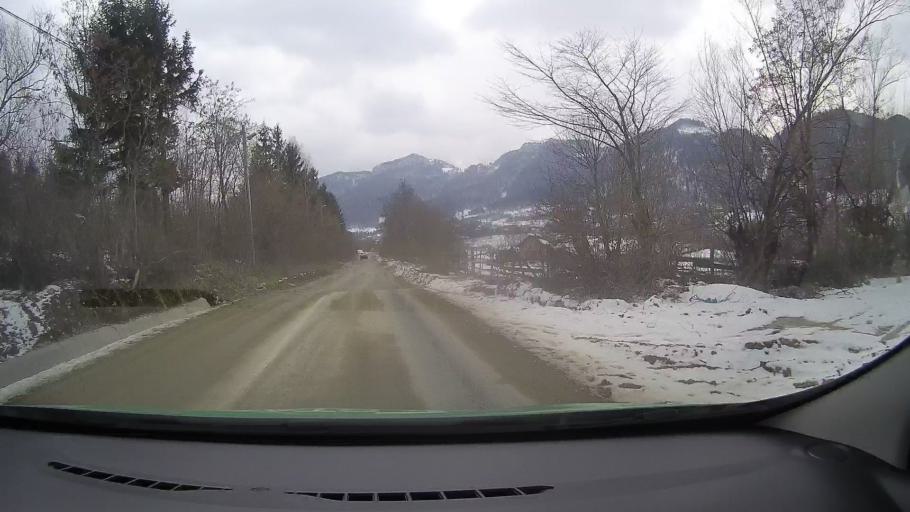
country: RO
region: Brasov
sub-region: Comuna Zarnesti
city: Zarnesti
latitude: 45.5481
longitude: 25.3220
